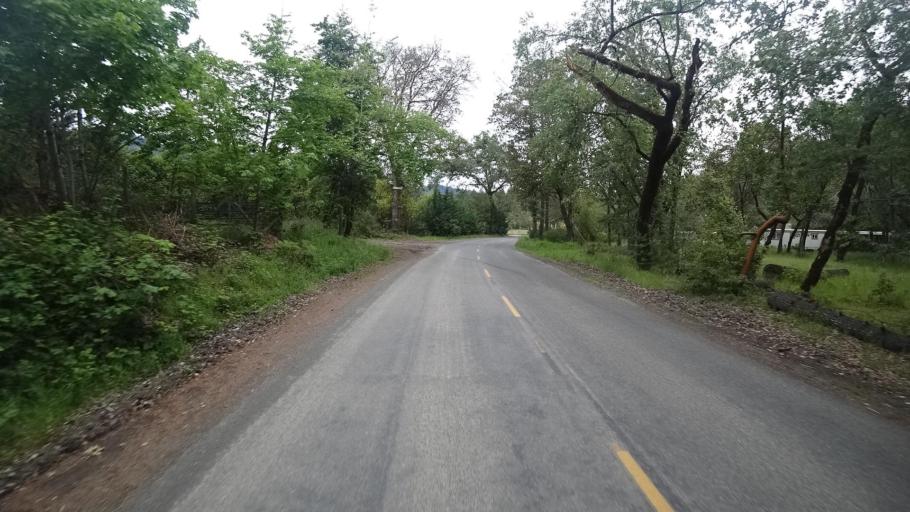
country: US
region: California
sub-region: Humboldt County
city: Willow Creek
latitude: 40.9590
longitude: -123.6302
